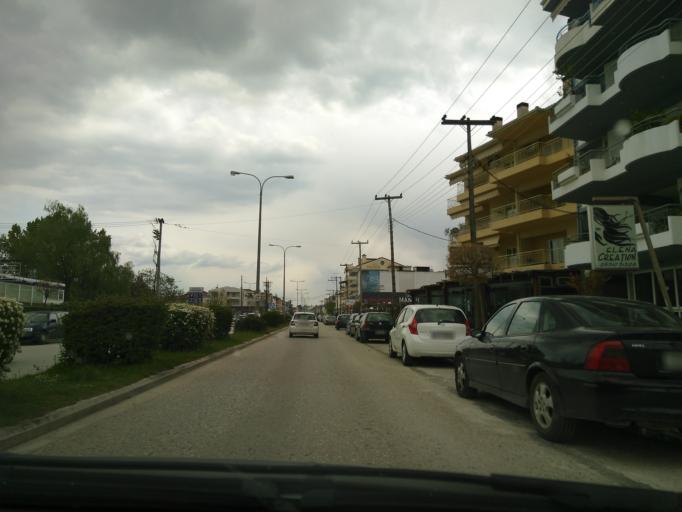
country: GR
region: Epirus
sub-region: Nomos Ioanninon
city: Ioannina
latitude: 39.6623
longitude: 20.8586
